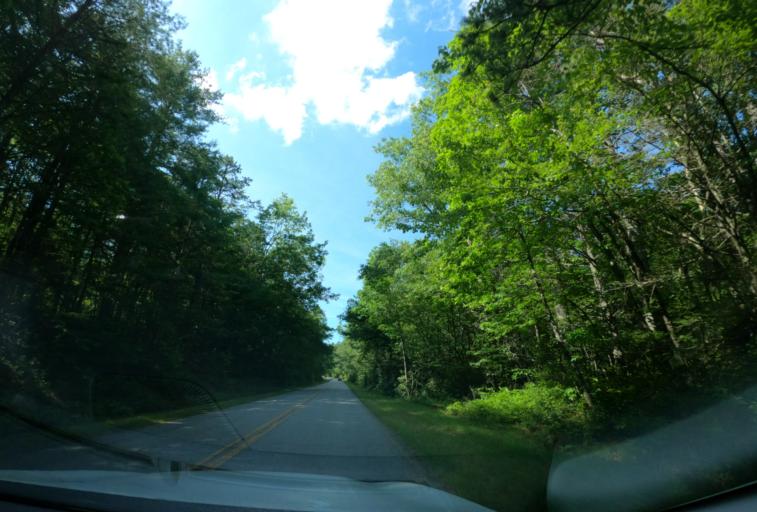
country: US
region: North Carolina
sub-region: Transylvania County
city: Brevard
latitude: 35.1737
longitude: -82.6388
